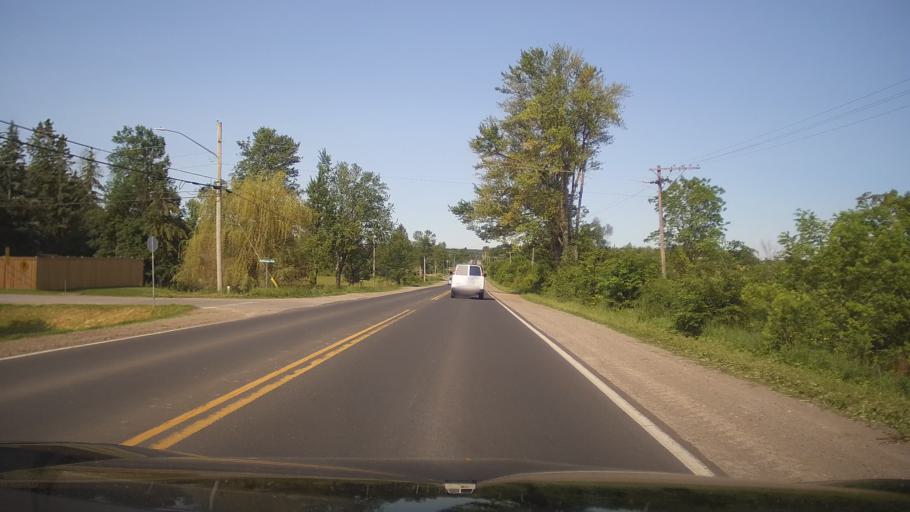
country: CA
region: Ontario
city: Peterborough
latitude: 44.2722
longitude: -78.3863
